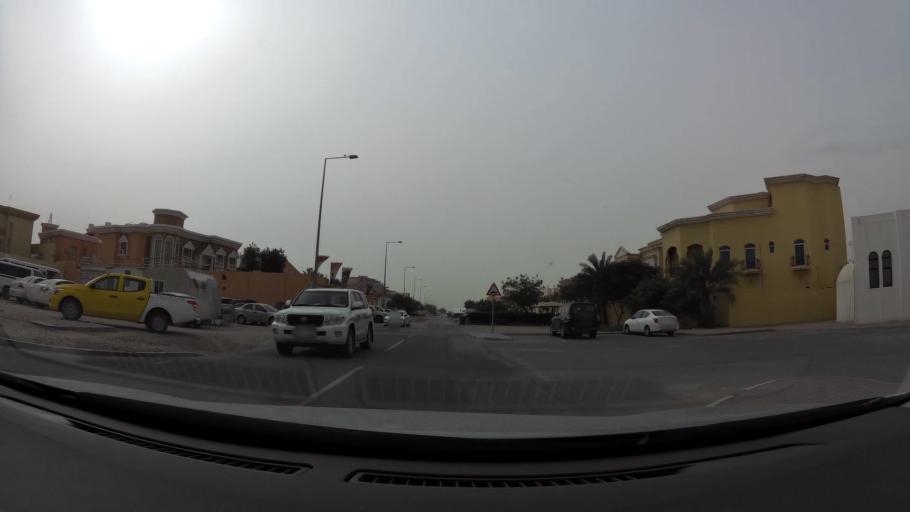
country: QA
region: Baladiyat ad Dawhah
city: Doha
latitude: 25.2504
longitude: 51.4977
